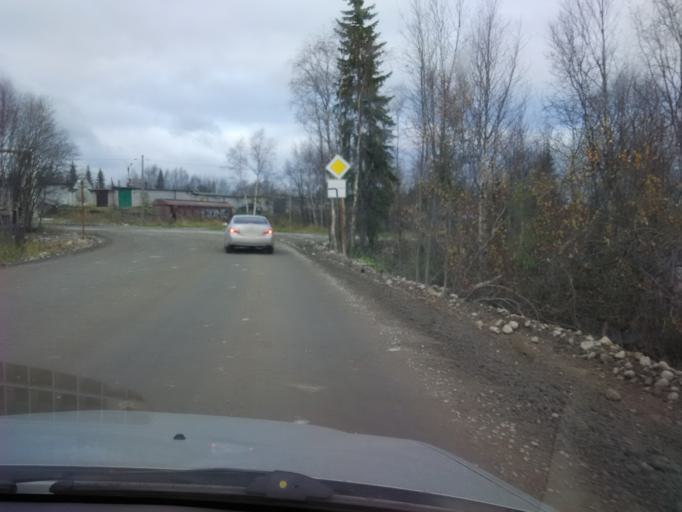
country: RU
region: Murmansk
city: Polyarnyye Zori
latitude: 67.3800
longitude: 32.5110
